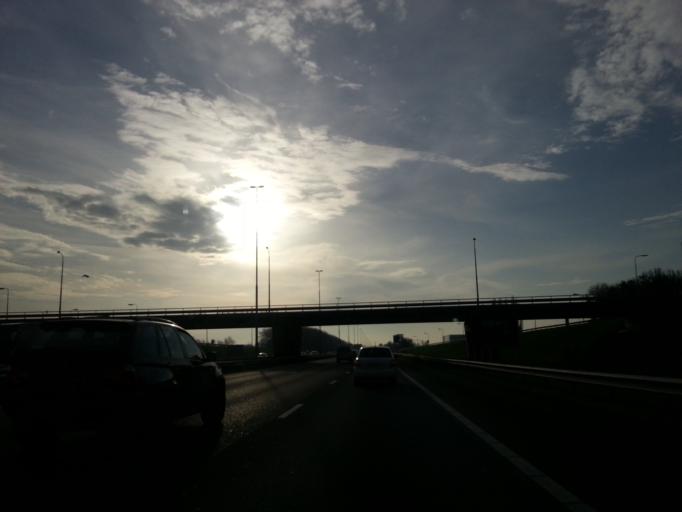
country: NL
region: South Holland
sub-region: Gemeente Delft
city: Delft
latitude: 51.9964
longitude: 4.3888
